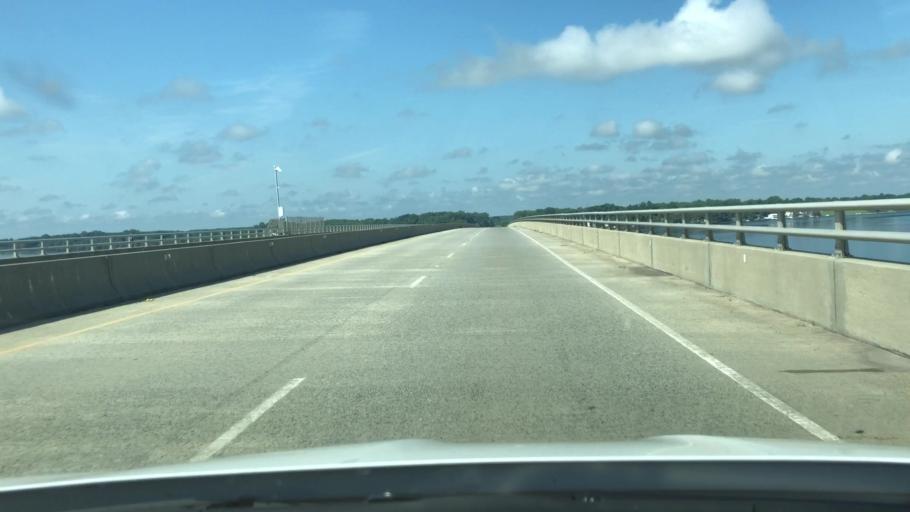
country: US
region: North Carolina
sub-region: Chowan County
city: Edenton
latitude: 36.0478
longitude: -76.6955
